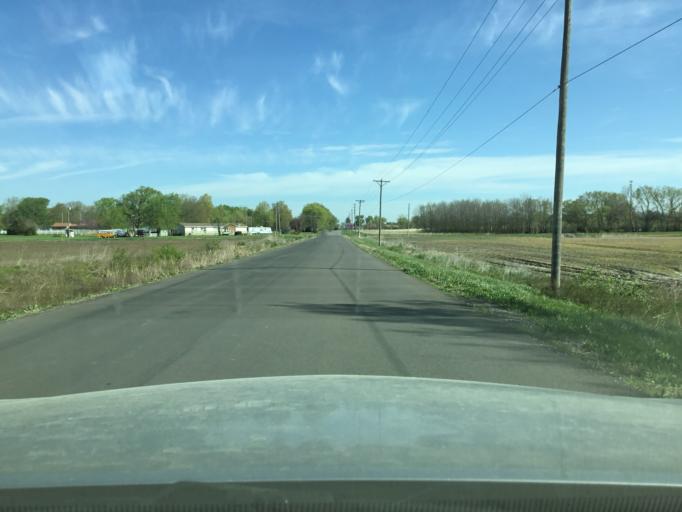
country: US
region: Kansas
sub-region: Neosho County
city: Chanute
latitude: 37.6587
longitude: -95.4435
